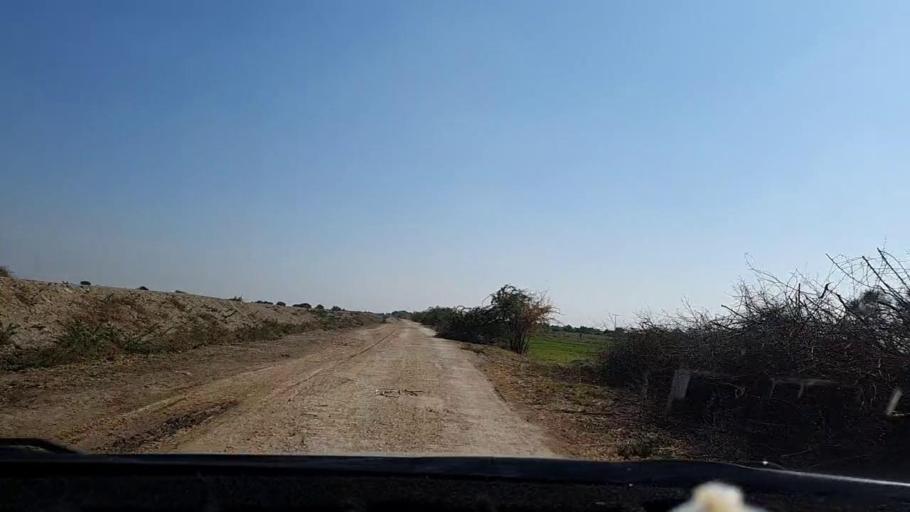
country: PK
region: Sindh
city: Tando Mittha Khan
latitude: 25.7711
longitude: 69.2947
